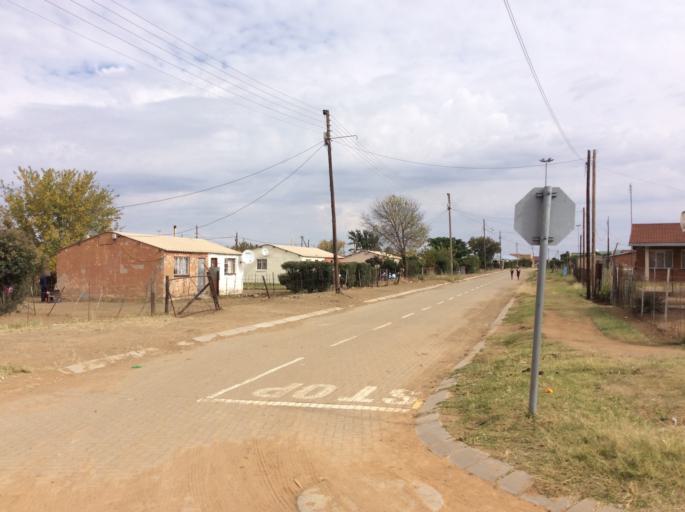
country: LS
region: Mafeteng
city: Mafeteng
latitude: -29.7219
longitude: 27.0118
